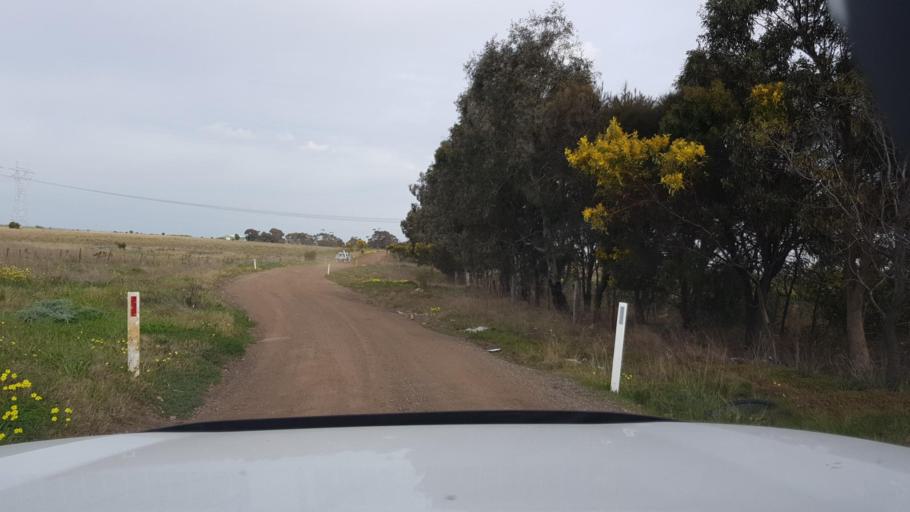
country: AU
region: Victoria
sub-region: Melton
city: Rockbank
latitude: -37.7701
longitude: 144.6455
